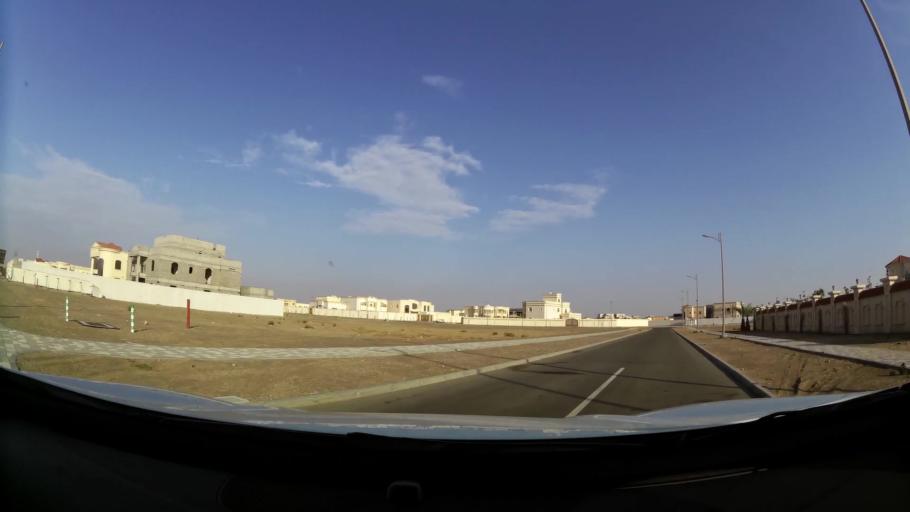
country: AE
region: Abu Dhabi
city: Al Ain
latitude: 24.1049
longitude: 55.8509
